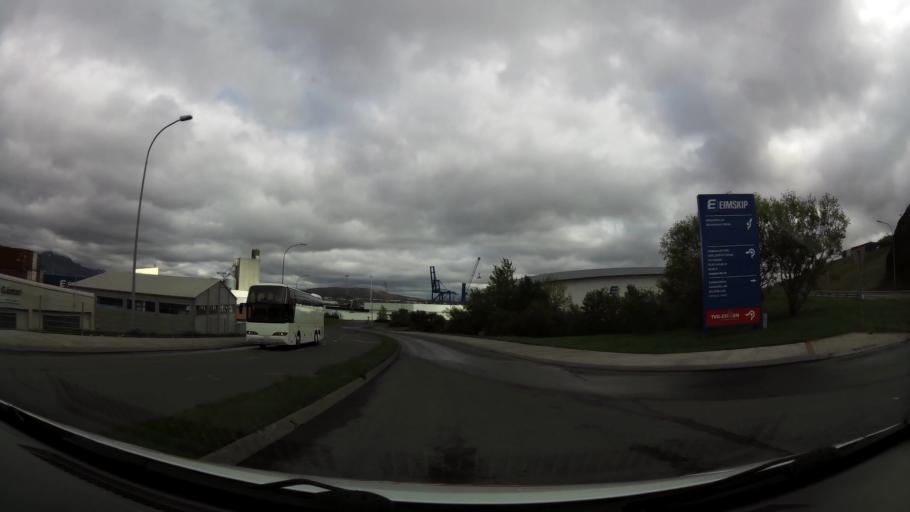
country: IS
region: Capital Region
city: Reykjavik
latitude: 64.1508
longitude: -21.8662
